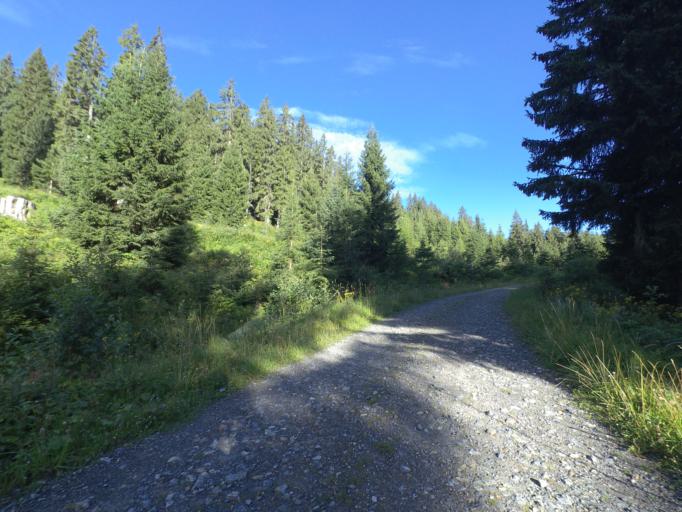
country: AT
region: Salzburg
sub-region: Politischer Bezirk Sankt Johann im Pongau
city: Goldegg
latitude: 47.3533
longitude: 13.0943
